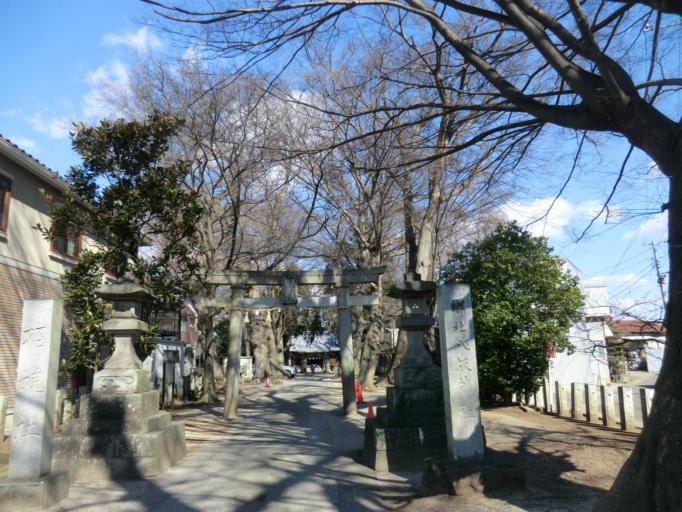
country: JP
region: Ibaraki
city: Naka
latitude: 36.0984
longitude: 140.2004
